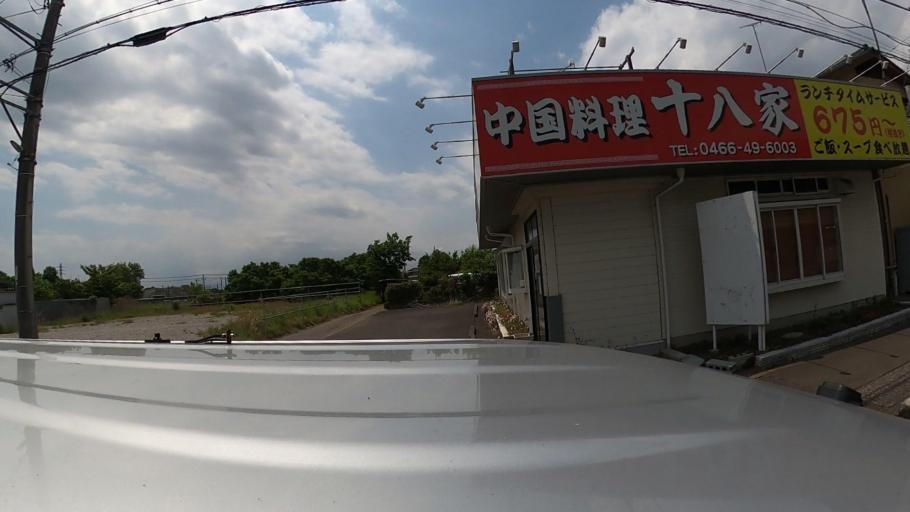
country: JP
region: Kanagawa
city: Chigasaki
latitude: 35.3847
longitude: 139.4017
